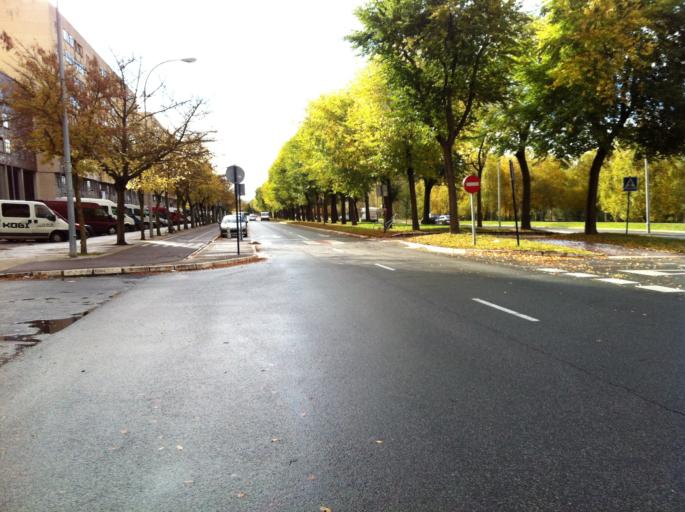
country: ES
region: Basque Country
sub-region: Provincia de Alava
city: Gasteiz / Vitoria
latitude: 42.8579
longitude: -2.6995
